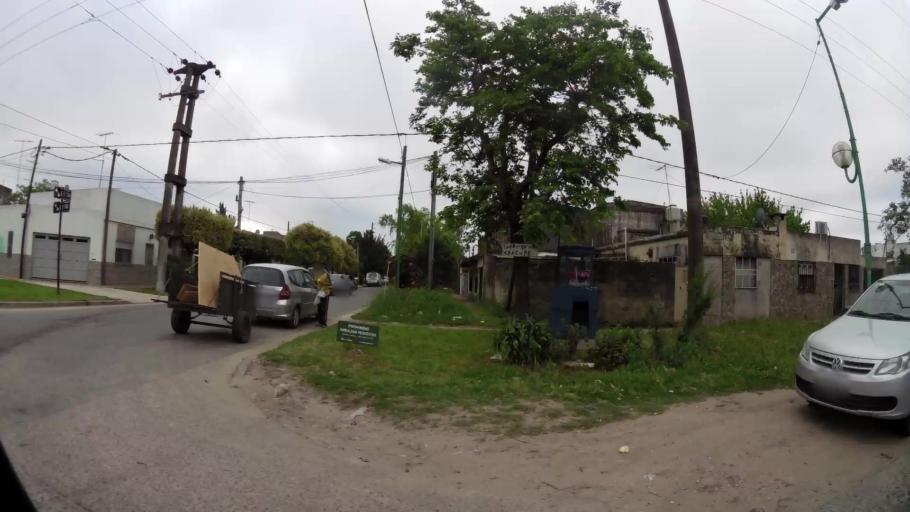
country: AR
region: Buenos Aires
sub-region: Partido de La Plata
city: La Plata
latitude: -34.9313
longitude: -57.9902
